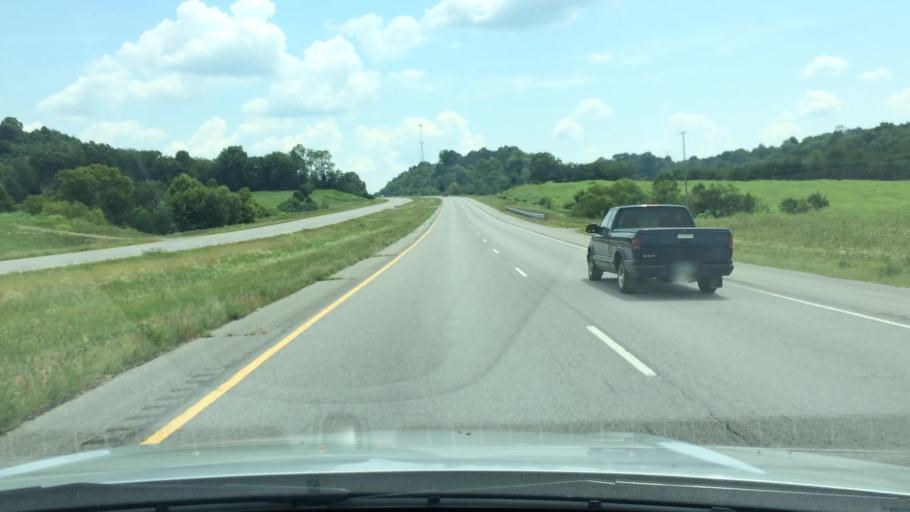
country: US
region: Tennessee
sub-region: Giles County
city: Pulaski
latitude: 35.1774
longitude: -86.9604
